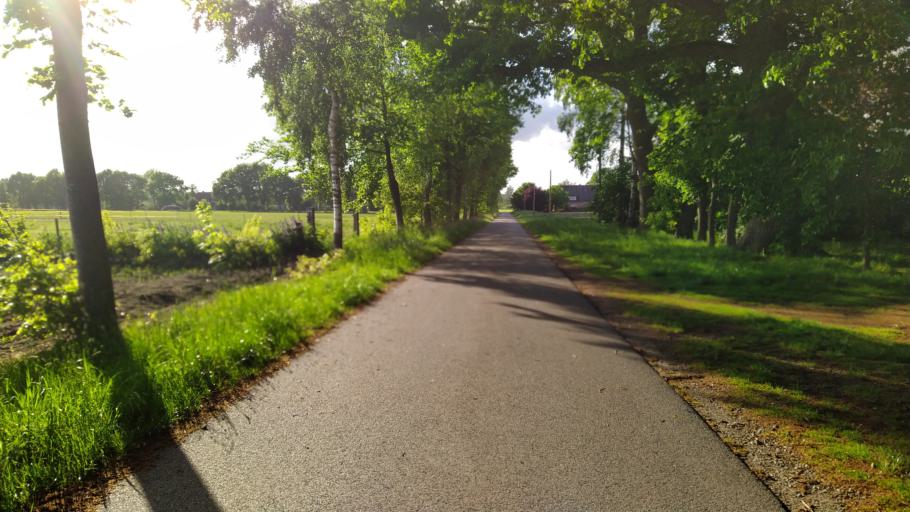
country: DE
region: Lower Saxony
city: Farven
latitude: 53.4497
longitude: 9.2793
